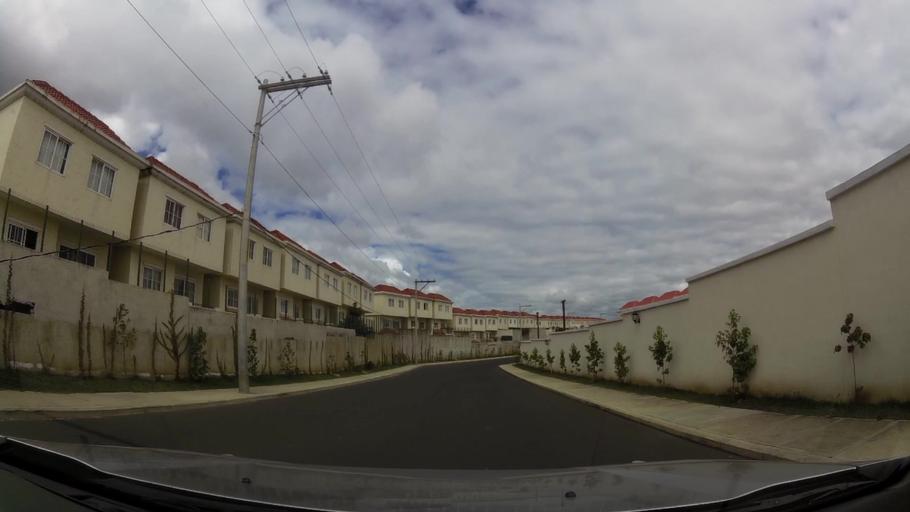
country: GT
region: Guatemala
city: Guatemala City
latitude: 14.6731
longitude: -90.5588
